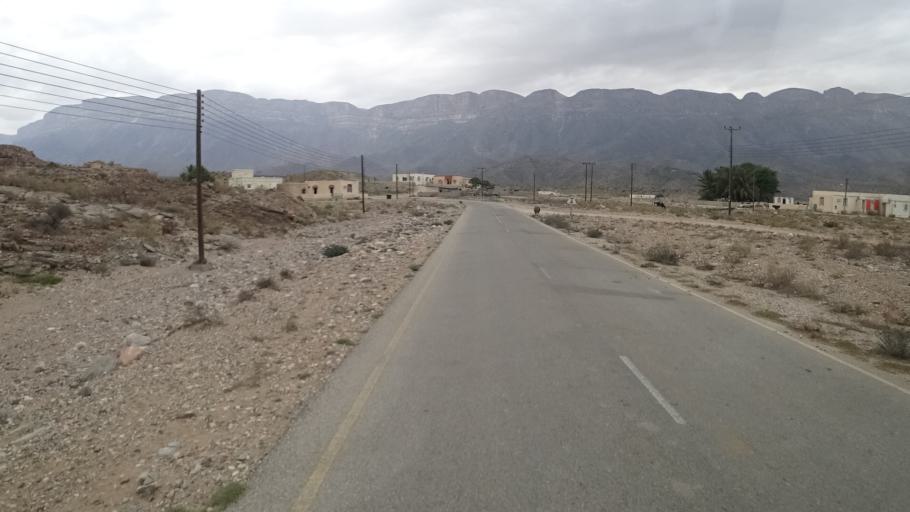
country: OM
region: Zufar
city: Salalah
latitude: 17.1650
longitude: 54.9813
